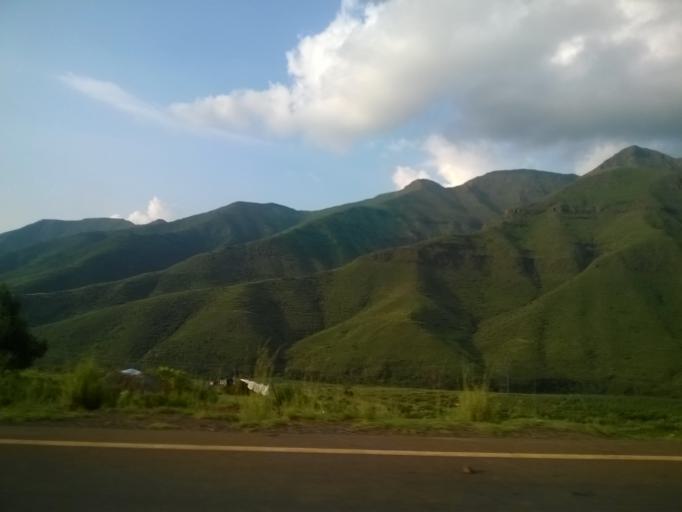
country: LS
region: Butha-Buthe
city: Butha-Buthe
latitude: -29.0507
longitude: 28.3346
